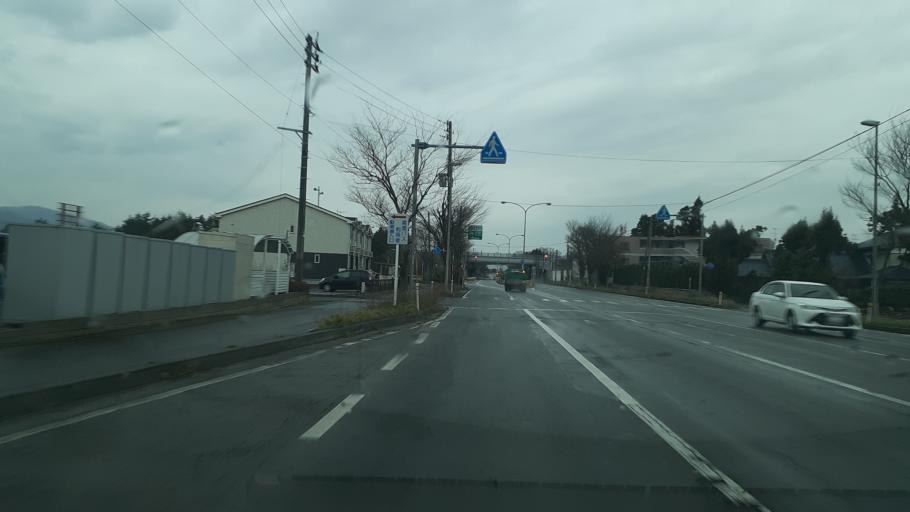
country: JP
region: Niigata
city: Gosen
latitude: 37.7613
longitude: 139.2329
